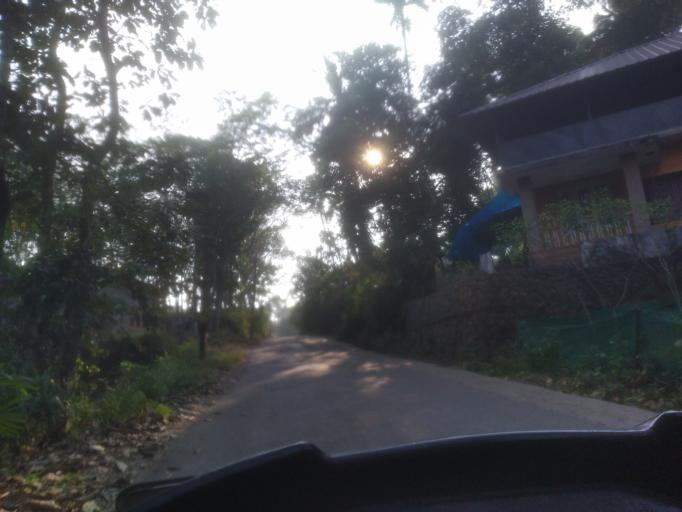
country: IN
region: Kerala
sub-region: Ernakulam
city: Piravam
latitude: 9.8107
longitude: 76.4963
